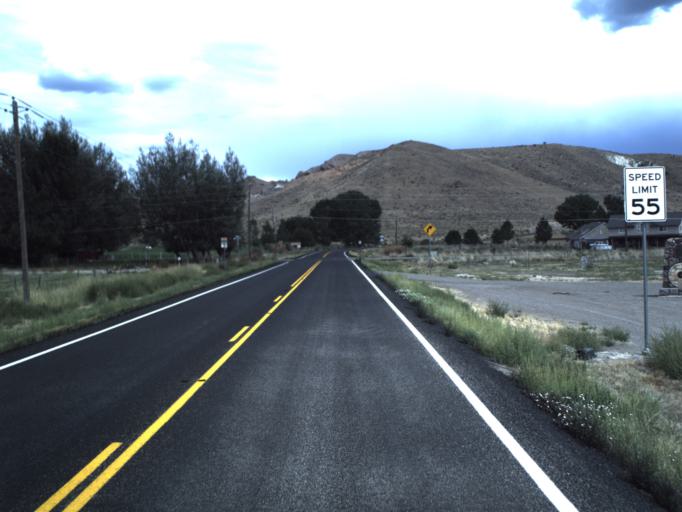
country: US
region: Utah
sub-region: Sevier County
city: Richfield
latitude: 38.7745
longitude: -111.9919
